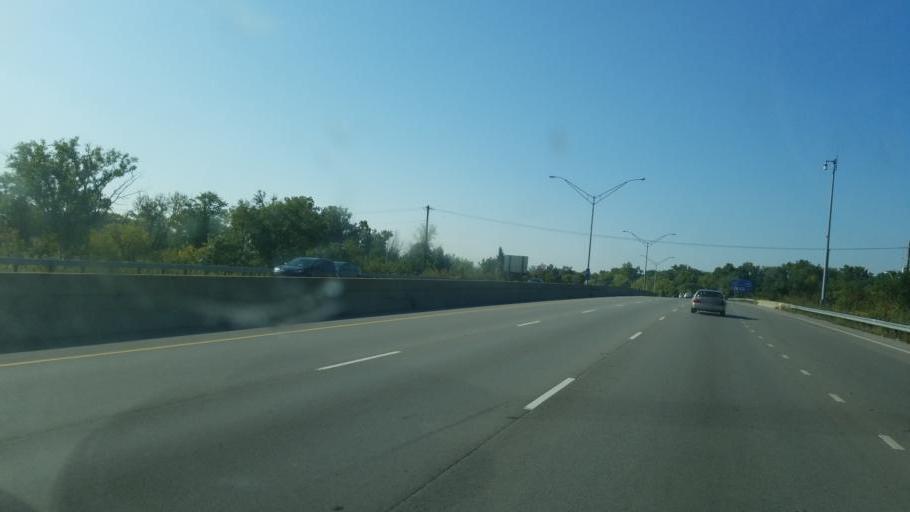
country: US
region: Ohio
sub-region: Franklin County
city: Worthington
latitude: 40.0528
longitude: -83.0325
